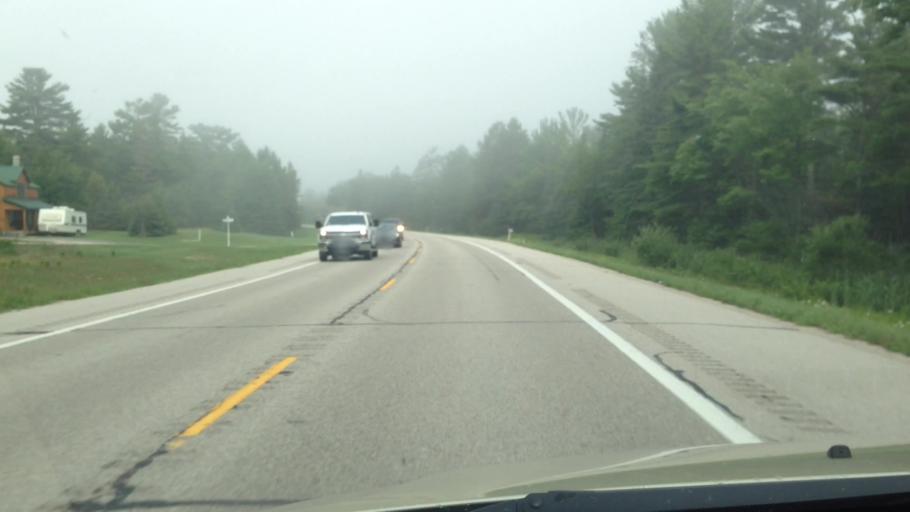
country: US
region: Michigan
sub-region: Luce County
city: Newberry
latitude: 46.1044
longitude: -85.4221
